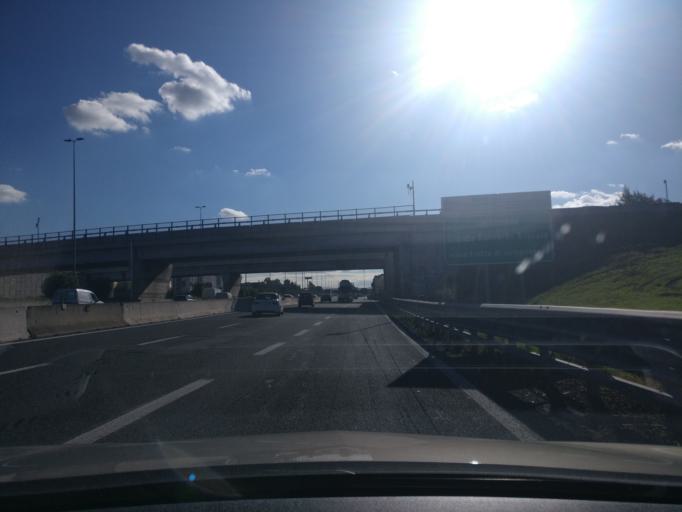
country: IT
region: Latium
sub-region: Citta metropolitana di Roma Capitale
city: Ciampino
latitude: 41.8540
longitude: 12.5973
